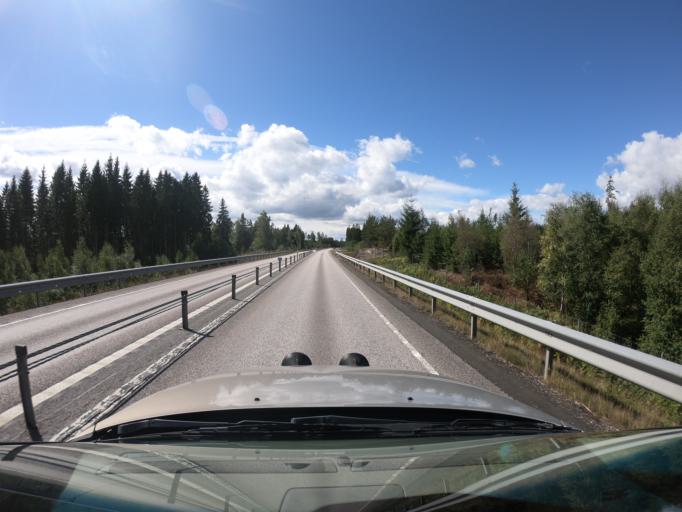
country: SE
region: Kronoberg
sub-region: Vaxjo Kommun
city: Braas
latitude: 57.0050
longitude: 15.0393
